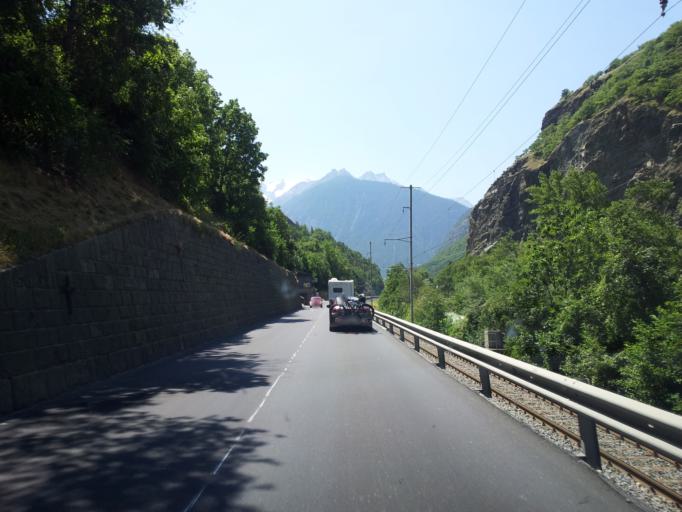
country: CH
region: Valais
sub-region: Visp District
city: Visp
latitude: 46.2747
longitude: 7.8821
